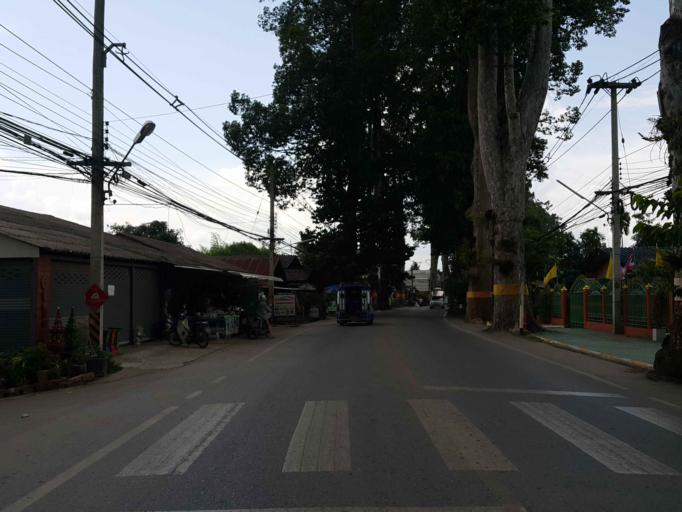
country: TH
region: Chiang Mai
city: Saraphi
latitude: 18.7055
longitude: 99.0399
